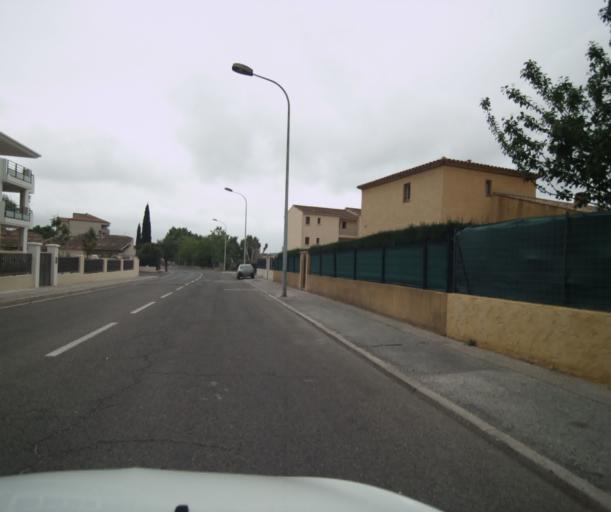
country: FR
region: Provence-Alpes-Cote d'Azur
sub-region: Departement du Var
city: La Garde
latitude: 43.1235
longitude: 6.0007
